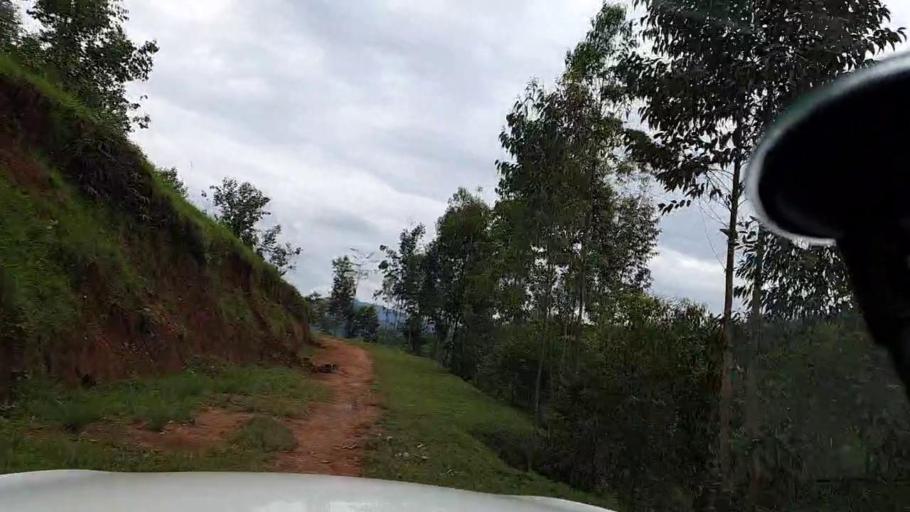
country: RW
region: Southern Province
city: Gitarama
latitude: -2.0845
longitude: 29.6488
